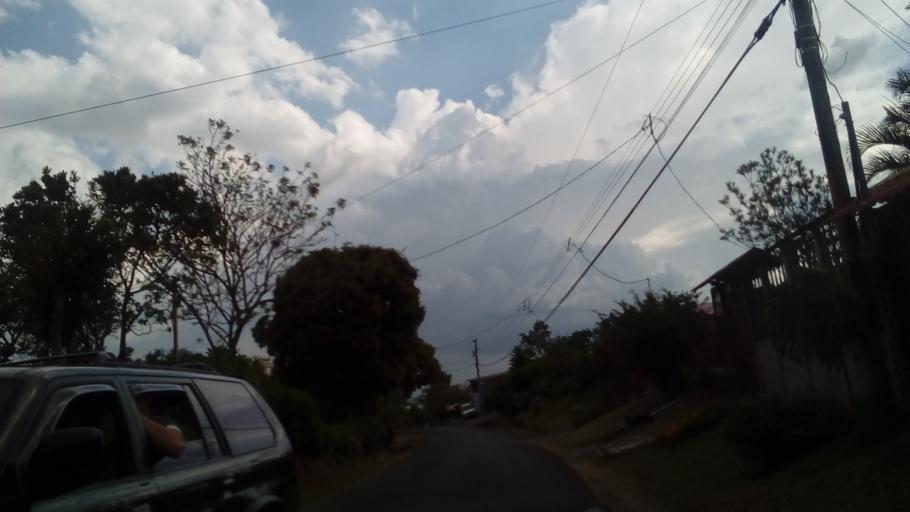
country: CR
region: Alajuela
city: San Juan
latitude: 10.1048
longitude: -84.2728
